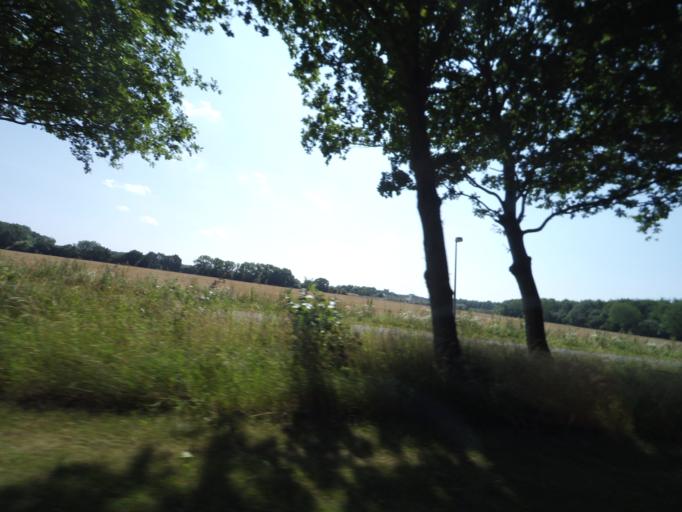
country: DK
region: South Denmark
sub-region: Odense Kommune
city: Neder Holluf
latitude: 55.3737
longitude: 10.4149
